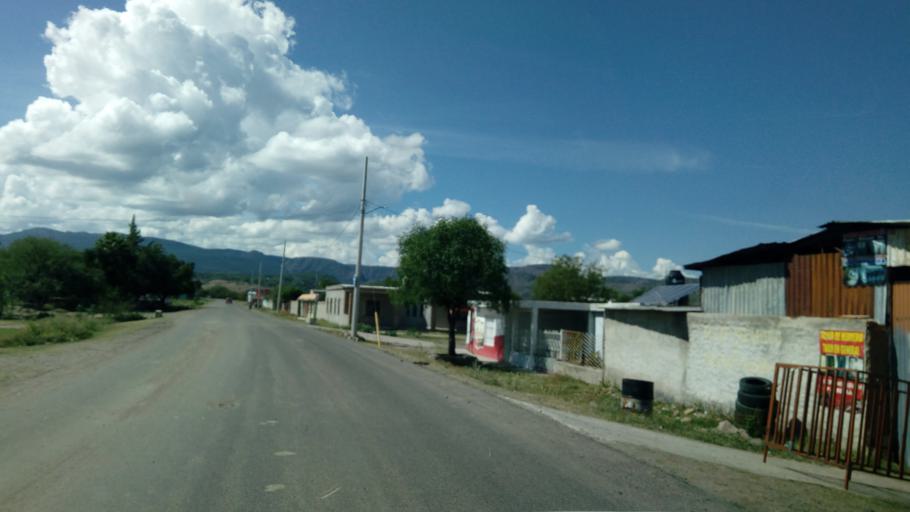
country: MX
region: Durango
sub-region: Durango
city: Jose Refugio Salcido
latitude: 23.8490
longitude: -104.4781
